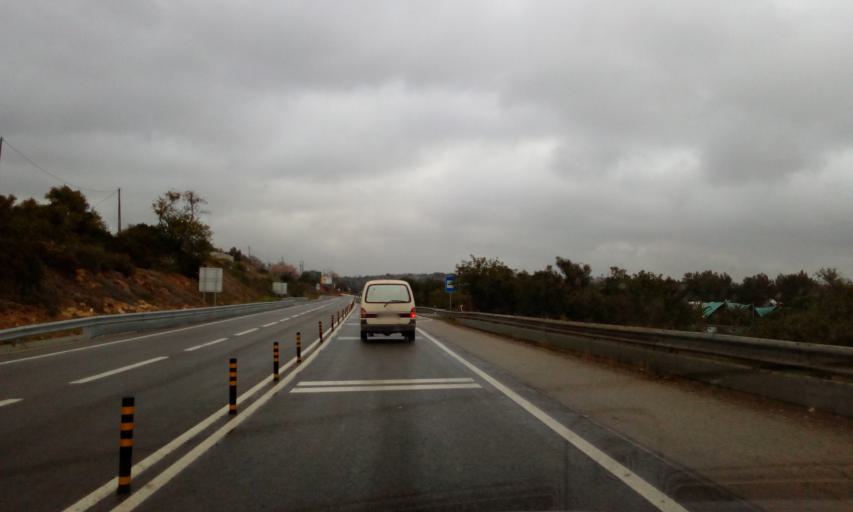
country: PT
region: Faro
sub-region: Albufeira
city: Guia
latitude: 37.1252
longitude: -8.3173
